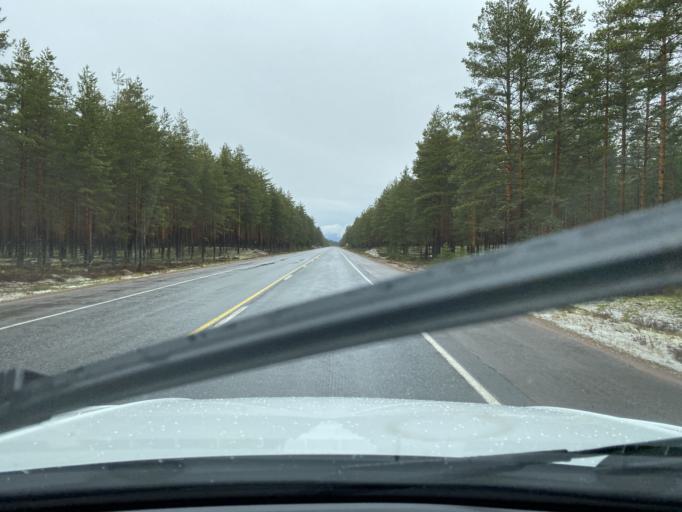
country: FI
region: Satakunta
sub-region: Pori
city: Vampula
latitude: 60.9688
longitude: 22.6811
